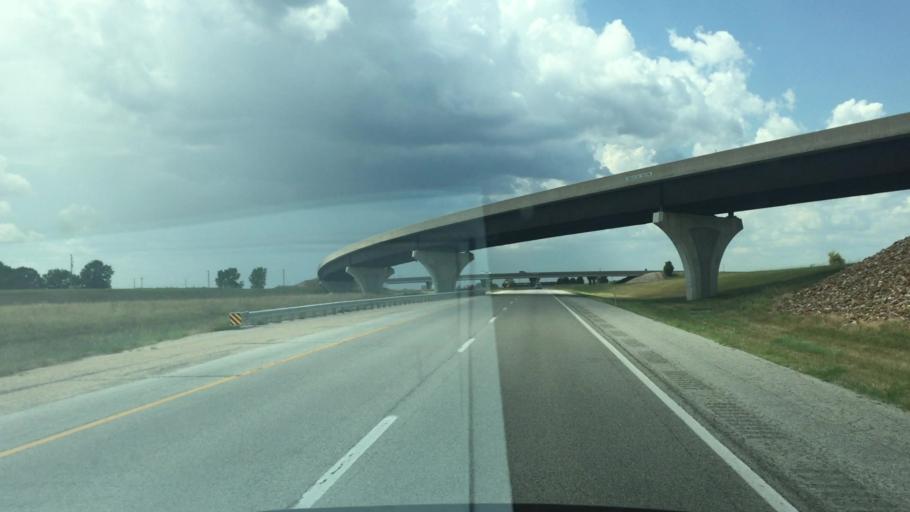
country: US
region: Kansas
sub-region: Shawnee County
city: Topeka
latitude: 39.0314
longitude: -95.6086
